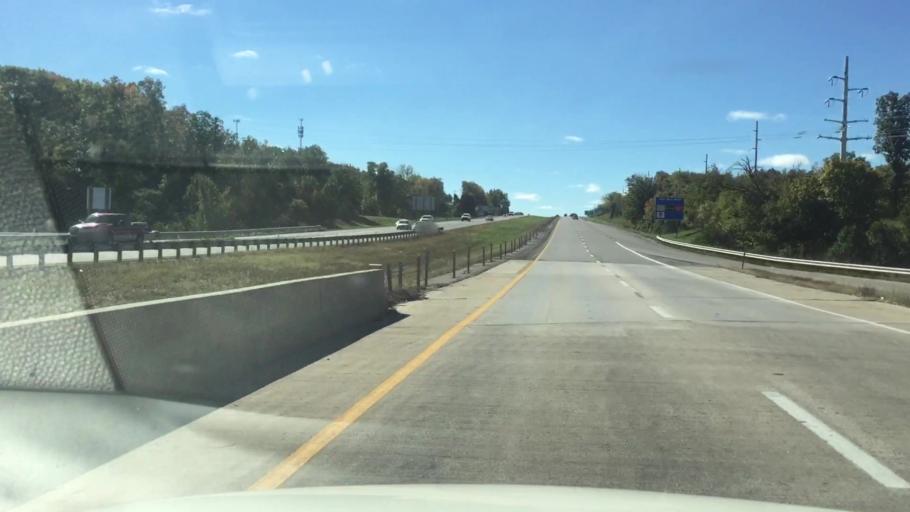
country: US
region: Missouri
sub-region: Boone County
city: Columbia
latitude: 38.9438
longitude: -92.2939
